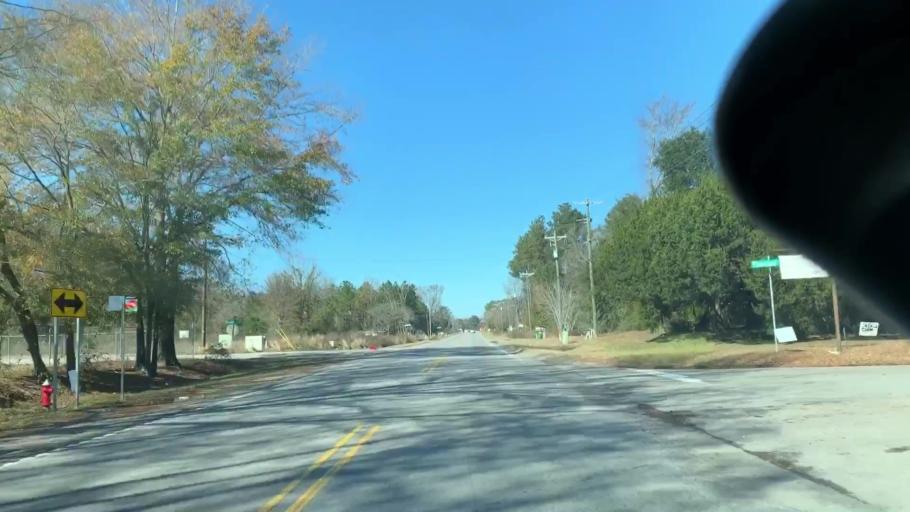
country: US
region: South Carolina
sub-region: Richland County
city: Hopkins
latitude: 33.9282
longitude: -80.9642
